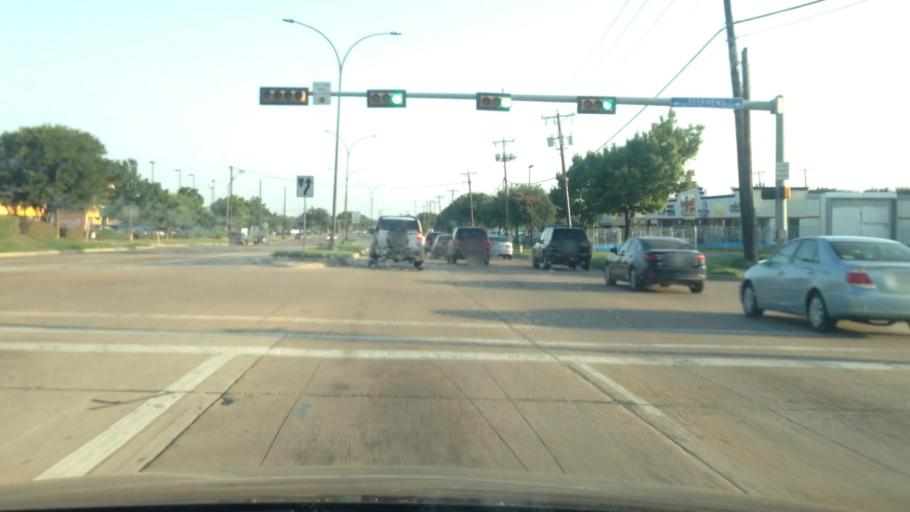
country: US
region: Texas
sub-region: Tarrant County
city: Dalworthington Gardens
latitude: 32.6742
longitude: -97.1150
